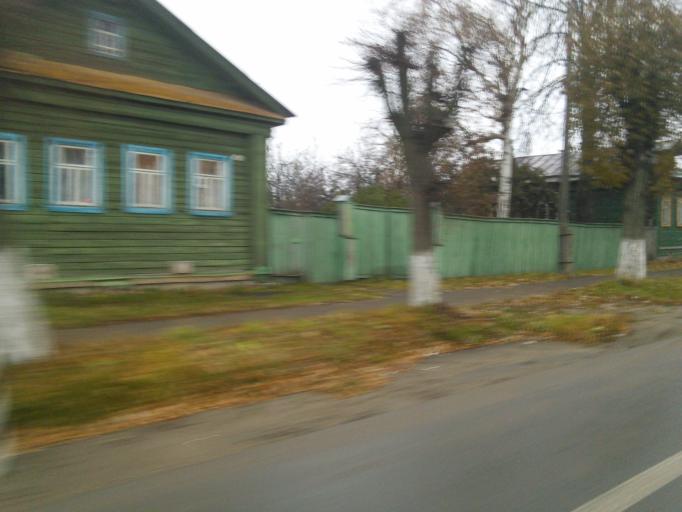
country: RU
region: Jaroslavl
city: Pereslavl'-Zalesskiy
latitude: 56.7282
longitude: 38.8438
